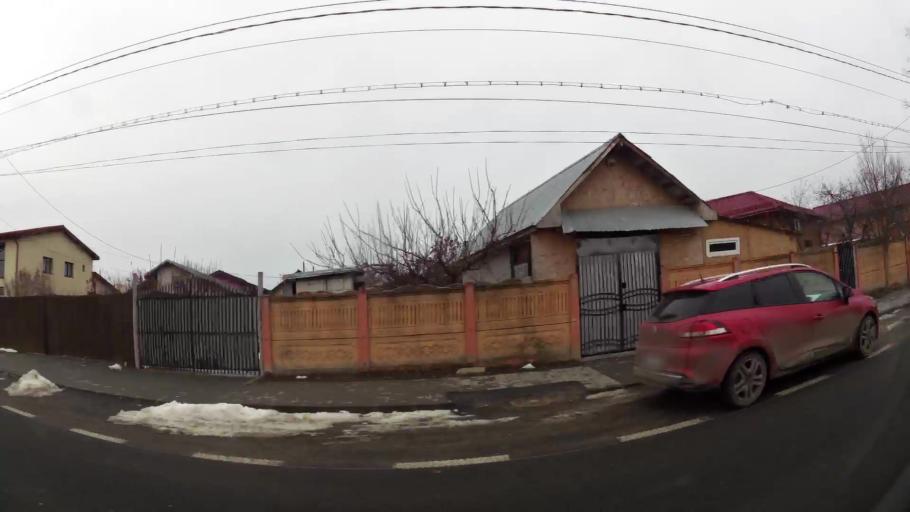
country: RO
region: Ilfov
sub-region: Comuna Tunari
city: Tunari
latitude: 44.5482
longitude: 26.1438
